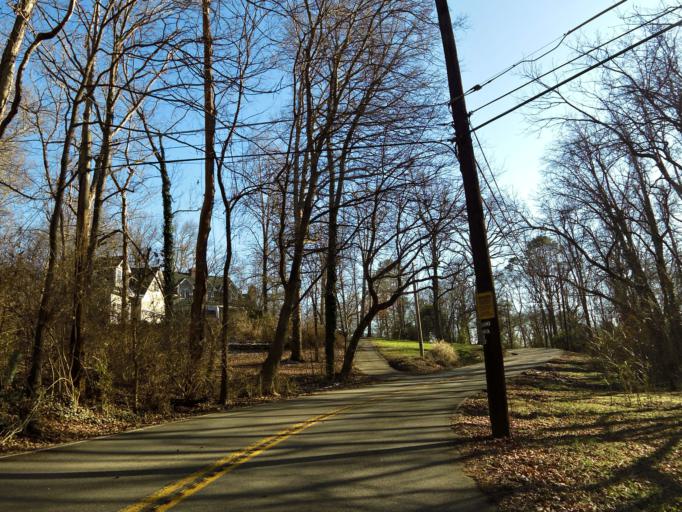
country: US
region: Tennessee
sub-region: Knox County
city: Knoxville
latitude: 35.8875
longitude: -83.9720
